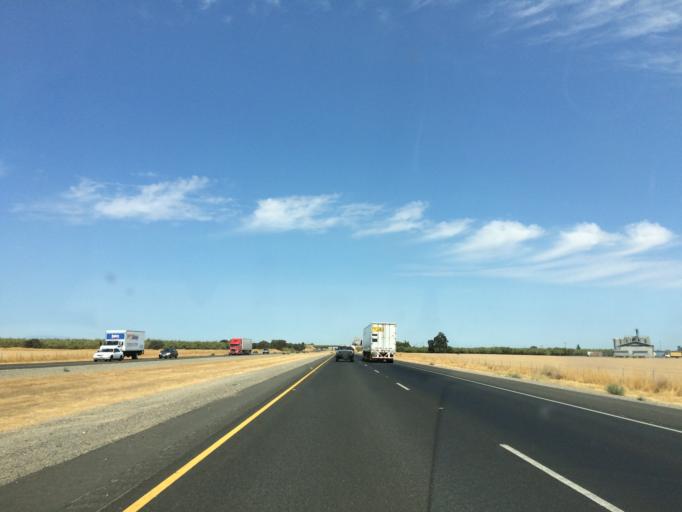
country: US
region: California
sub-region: Colusa County
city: Arbuckle
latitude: 38.9587
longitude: -122.0210
